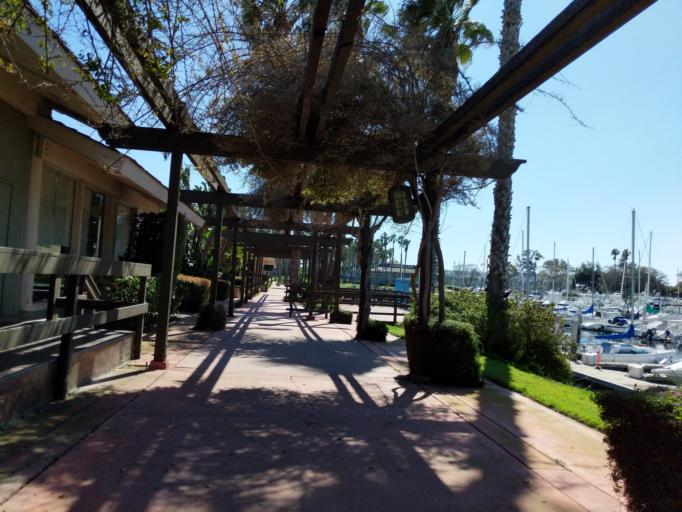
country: US
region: California
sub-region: San Diego County
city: San Diego
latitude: 32.7618
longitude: -117.2343
